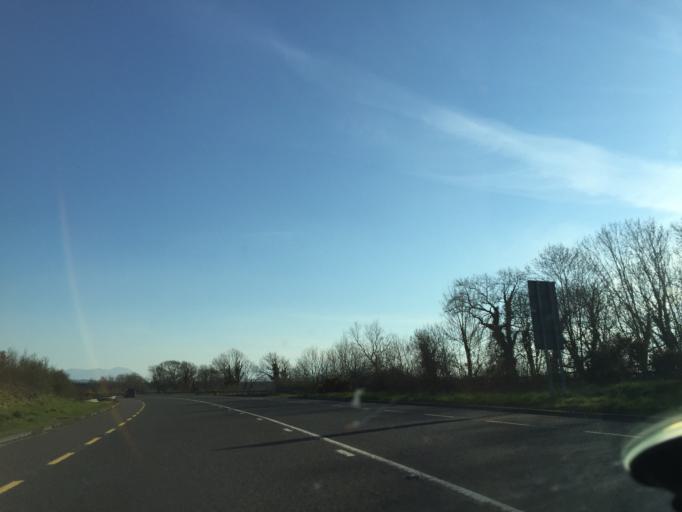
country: IE
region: Munster
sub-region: Ciarrai
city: Castleisland
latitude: 52.2014
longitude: -9.5706
